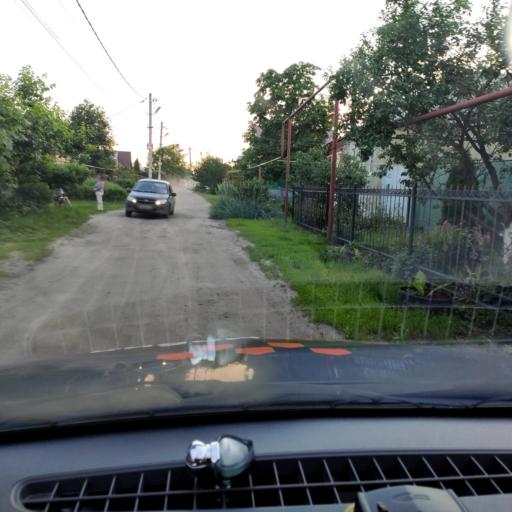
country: RU
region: Voronezj
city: Somovo
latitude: 51.7460
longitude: 39.3445
